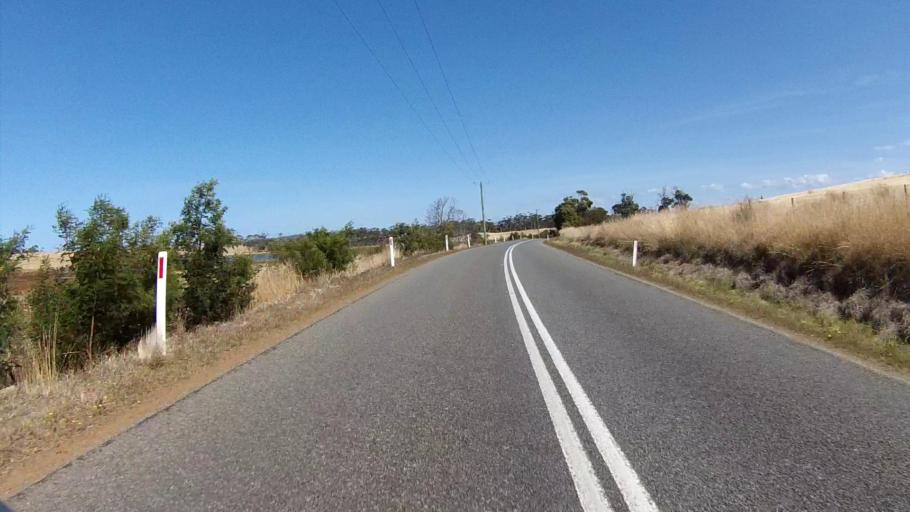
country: AU
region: Tasmania
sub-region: Sorell
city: Sorell
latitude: -42.2764
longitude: 148.0042
